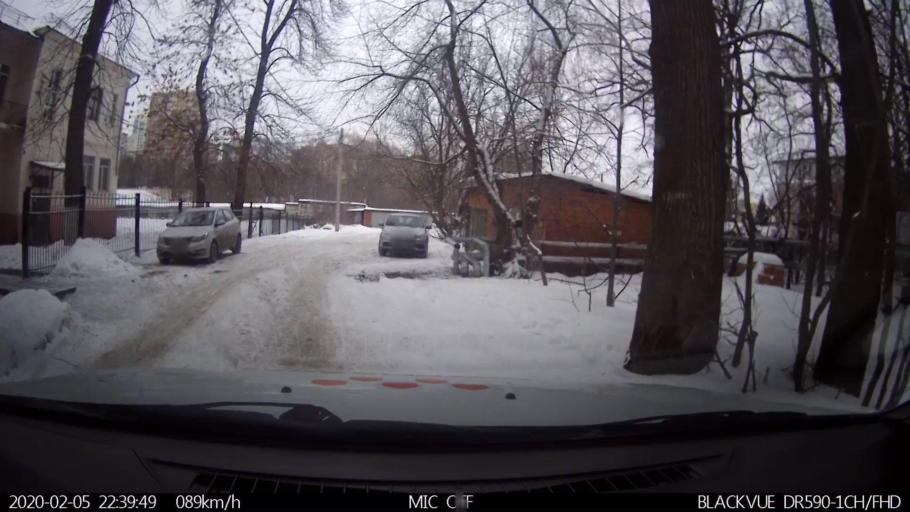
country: RU
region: Nizjnij Novgorod
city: Imeni Stepana Razina
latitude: 54.7255
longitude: 44.3095
